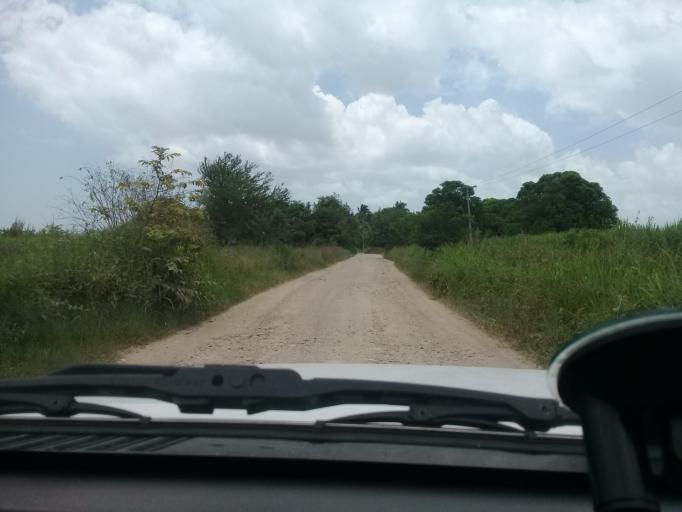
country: MX
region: Veracruz
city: Panuco
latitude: 22.1291
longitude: -98.0609
